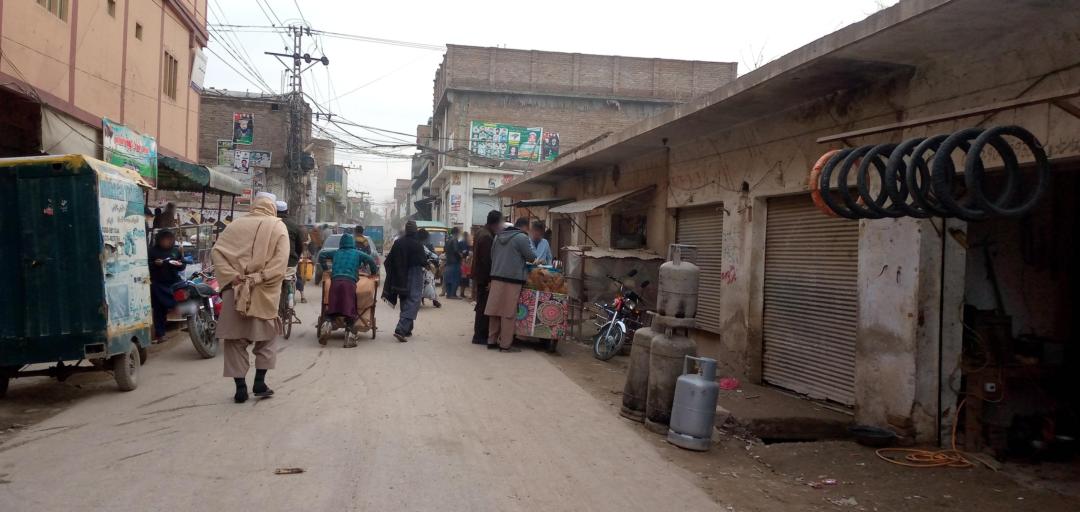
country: PK
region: Khyber Pakhtunkhwa
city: Peshawar
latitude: 34.0168
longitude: 71.4996
